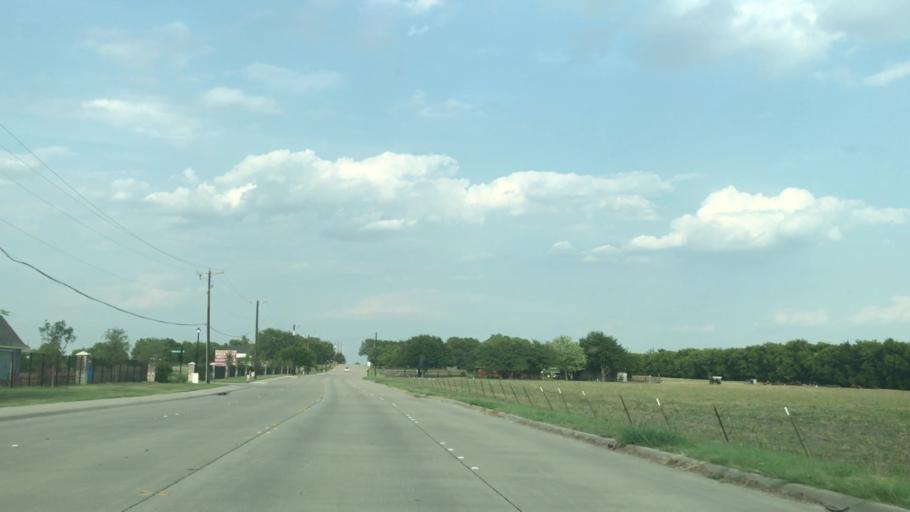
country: US
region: Texas
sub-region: Rockwall County
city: Rockwall
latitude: 32.9251
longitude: -96.4256
